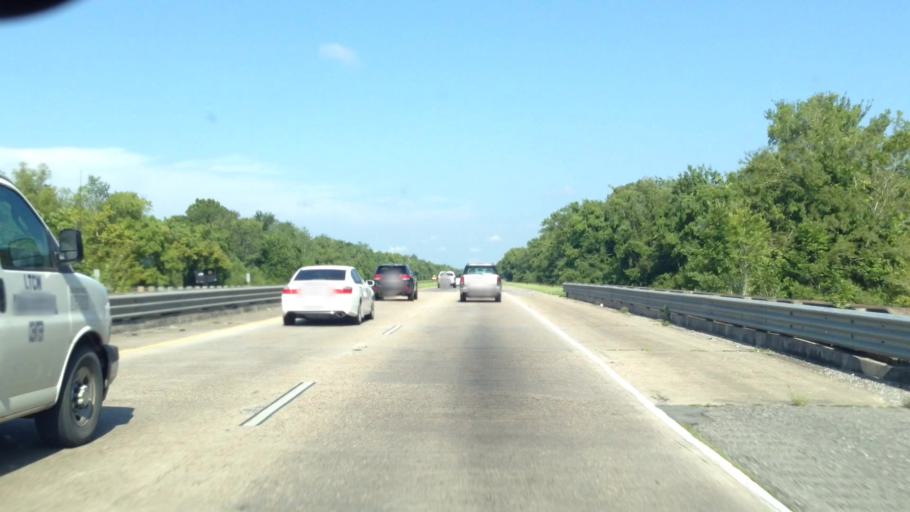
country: US
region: Louisiana
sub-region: Saint John the Baptist Parish
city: Reserve
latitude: 30.1132
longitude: -90.5804
